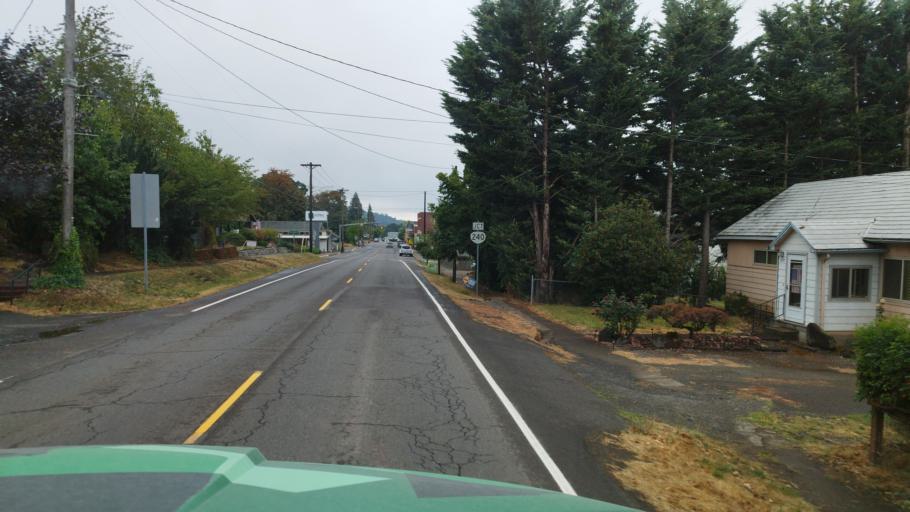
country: US
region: Oregon
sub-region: Yamhill County
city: Yamhill
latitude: 45.3432
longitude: -123.1879
